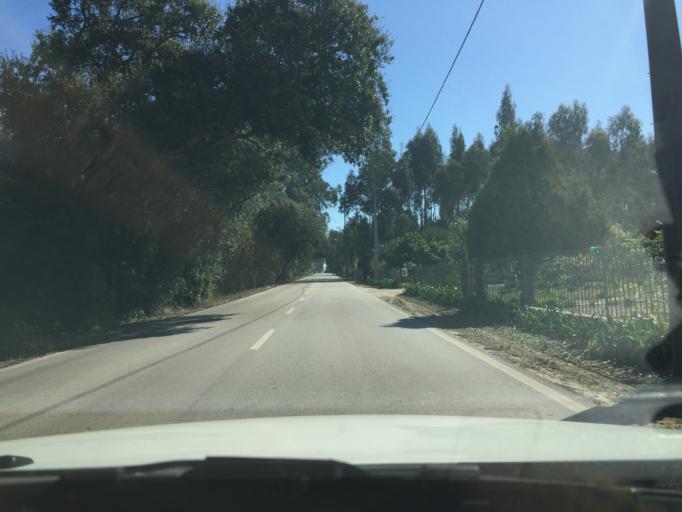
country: PT
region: Coimbra
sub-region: Cantanhede
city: Cantanhede
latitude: 40.4191
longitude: -8.5534
